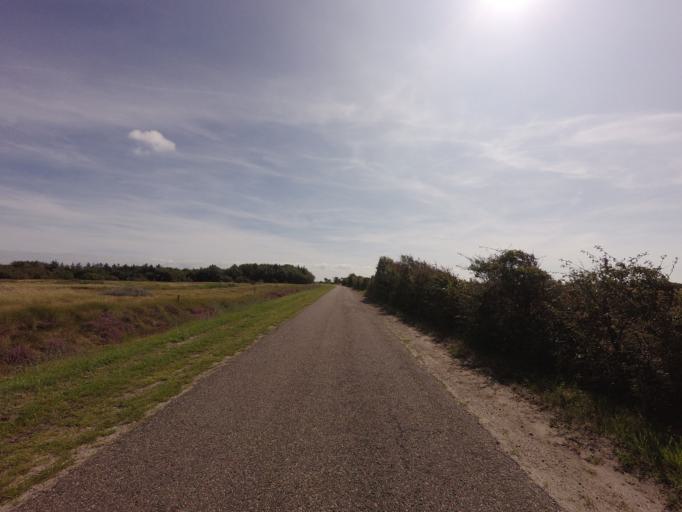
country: NL
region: Friesland
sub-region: Gemeente Ameland
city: Hollum
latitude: 53.4445
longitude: 5.6622
